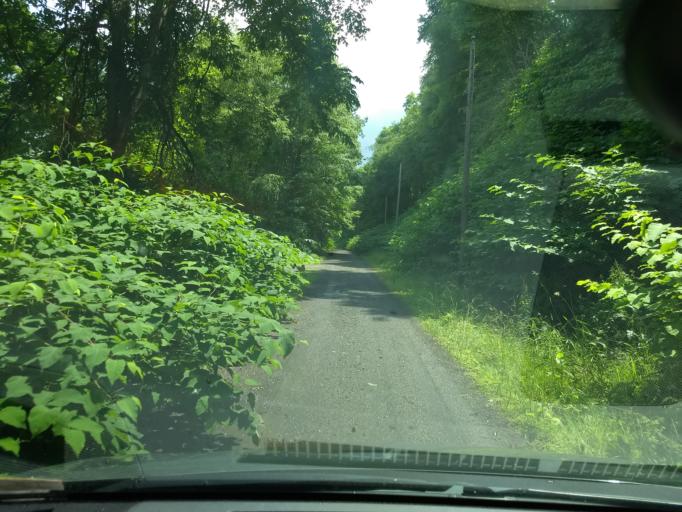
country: US
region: Pennsylvania
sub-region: Westmoreland County
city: Avonmore
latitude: 40.5252
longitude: -79.4993
